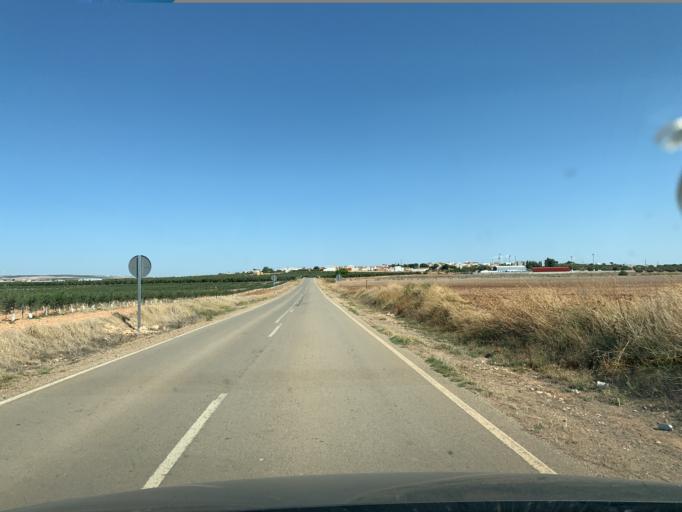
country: ES
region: Andalusia
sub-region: Provincia de Sevilla
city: La Lantejuela
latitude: 37.3483
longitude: -5.2404
